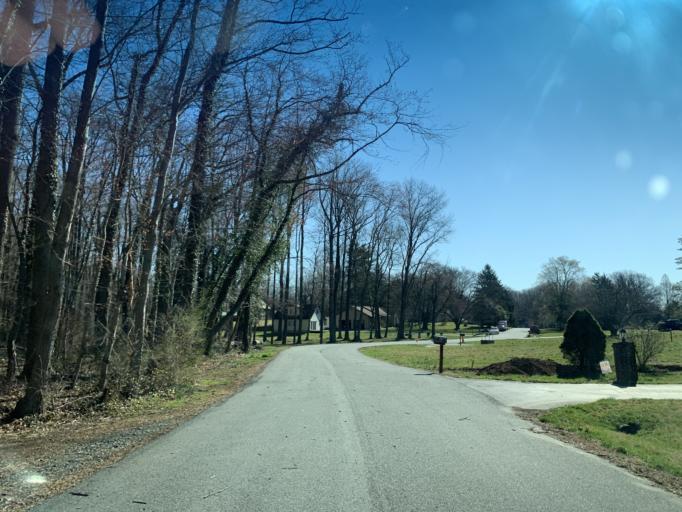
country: US
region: Maryland
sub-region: Harford County
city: Aberdeen
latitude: 39.5416
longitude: -76.2252
